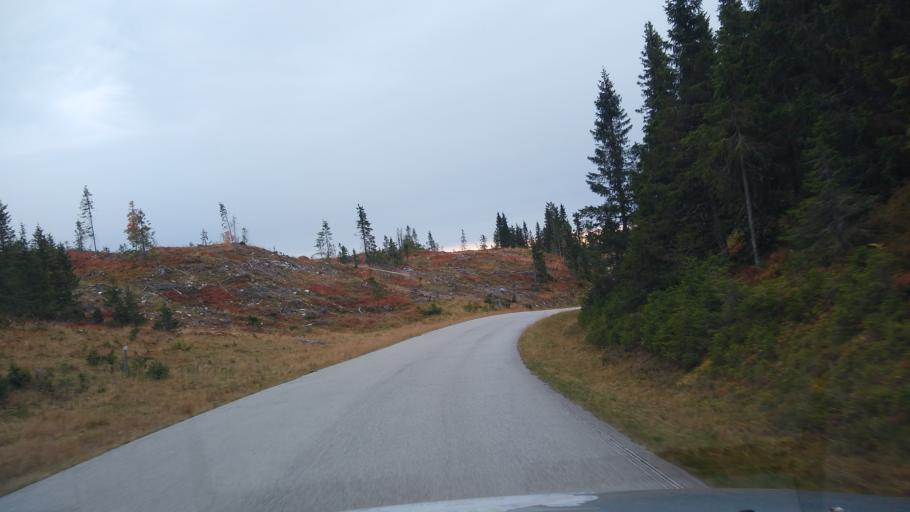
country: NO
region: Oppland
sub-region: Ringebu
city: Ringebu
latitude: 61.4763
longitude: 10.1276
